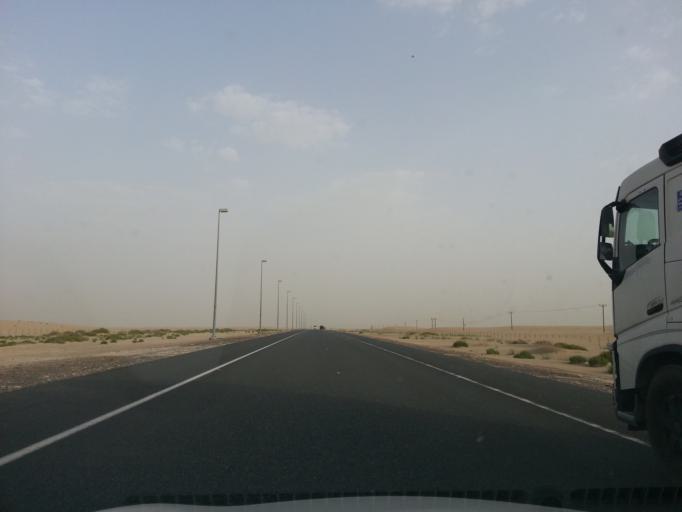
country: AE
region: Dubai
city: Dubai
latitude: 24.7162
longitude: 55.1278
